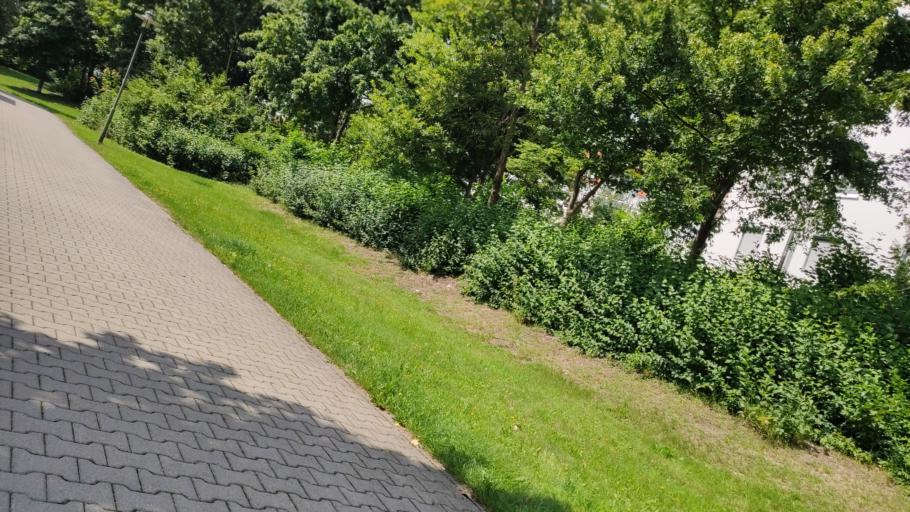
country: DE
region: Bavaria
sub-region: Swabia
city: Konigsbrunn
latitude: 48.2563
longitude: 10.8873
